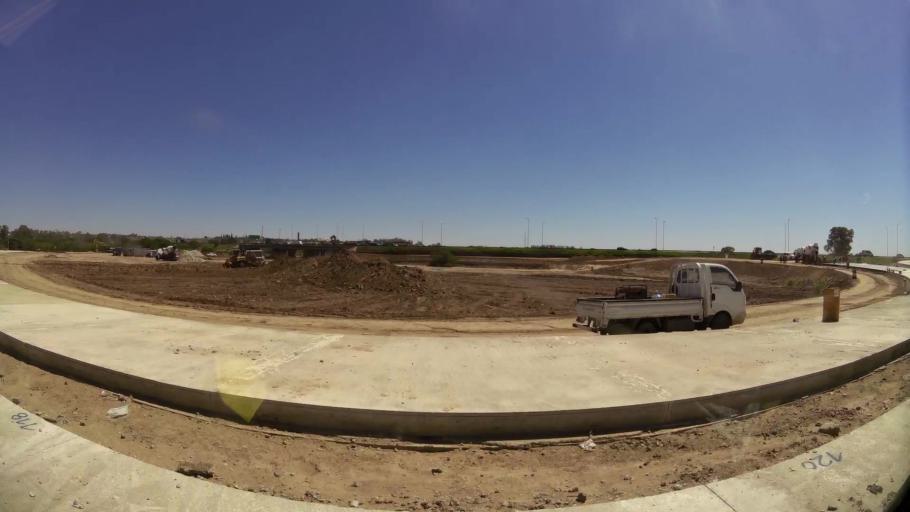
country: AR
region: Cordoba
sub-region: Departamento de Capital
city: Cordoba
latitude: -31.4091
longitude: -64.1239
